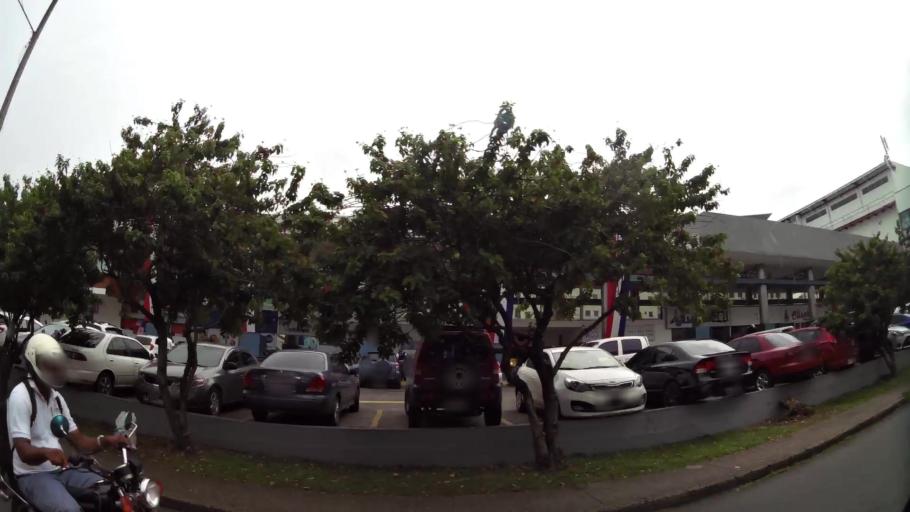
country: PA
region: Panama
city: Panama
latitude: 8.9909
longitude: -79.5212
